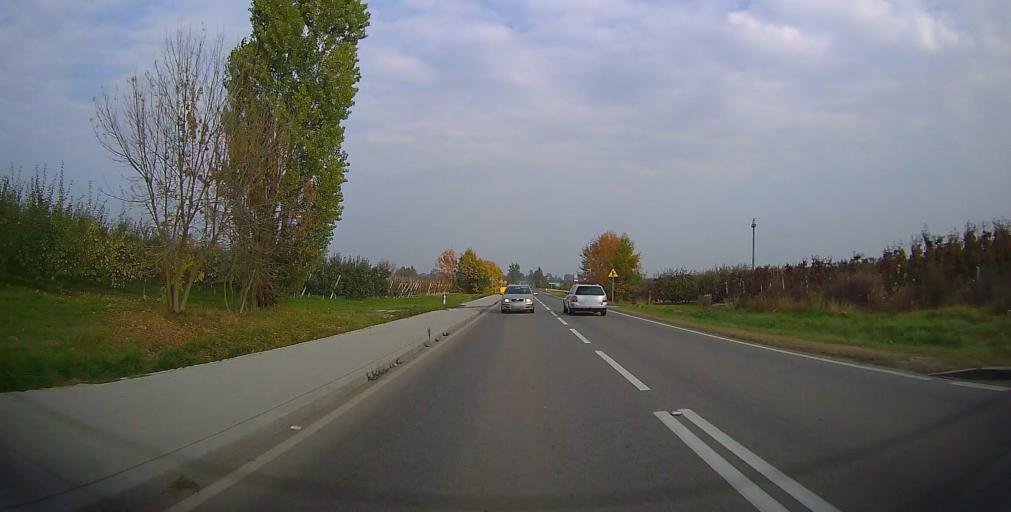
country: PL
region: Masovian Voivodeship
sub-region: Powiat grojecki
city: Bledow
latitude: 51.7644
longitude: 20.7675
